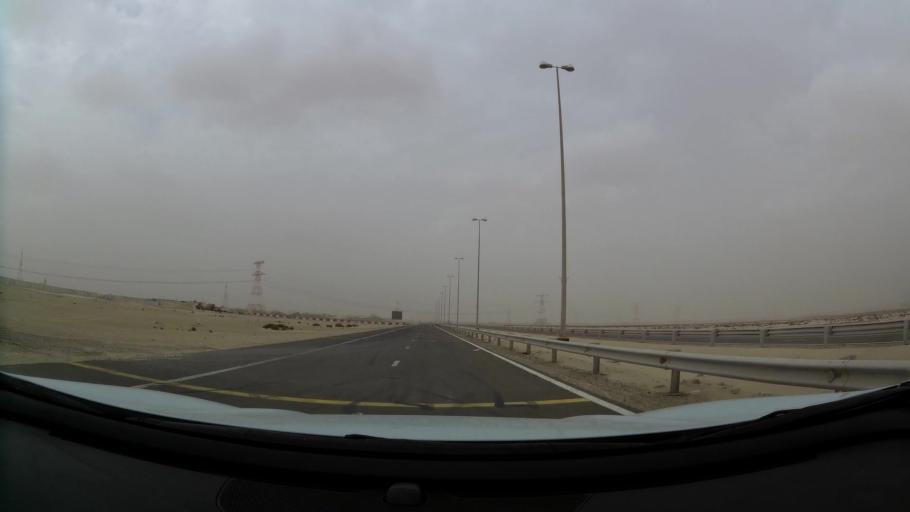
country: AE
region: Abu Dhabi
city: Abu Dhabi
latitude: 24.4323
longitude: 54.7640
